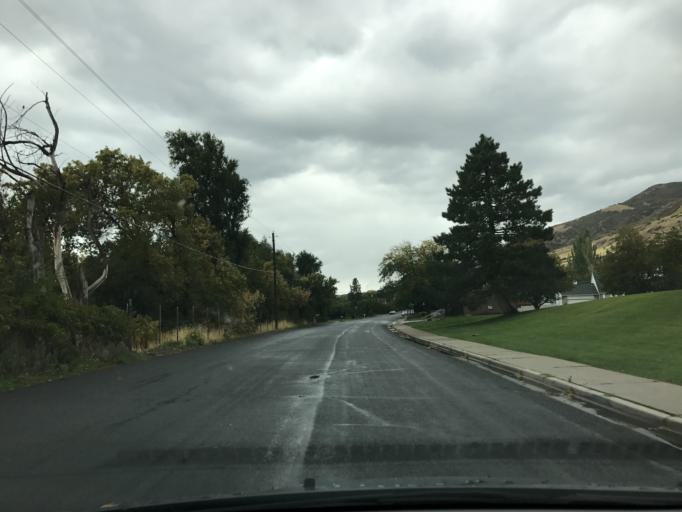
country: US
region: Utah
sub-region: Davis County
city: Farmington
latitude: 40.9943
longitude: -111.8939
